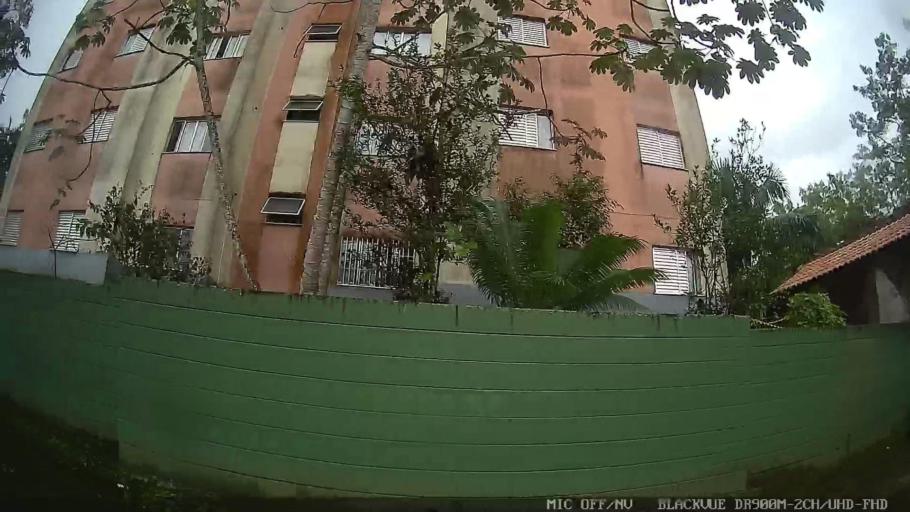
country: BR
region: Sao Paulo
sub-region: Itanhaem
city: Itanhaem
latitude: -24.1762
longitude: -46.8313
